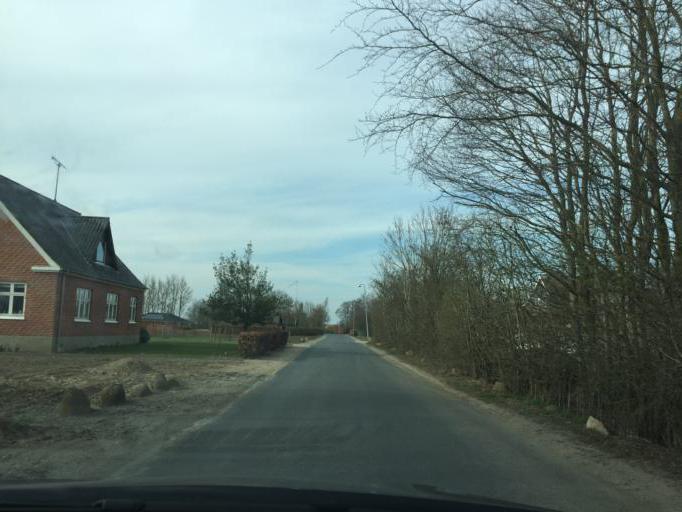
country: DK
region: South Denmark
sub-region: Faaborg-Midtfyn Kommune
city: Arslev
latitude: 55.3239
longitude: 10.5177
